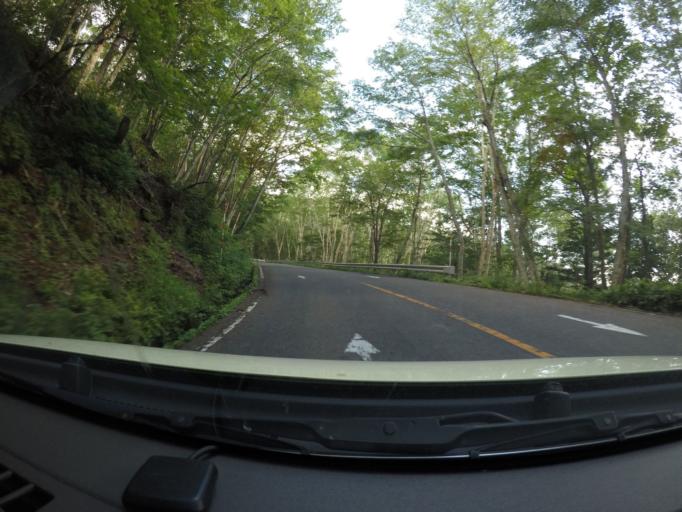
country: JP
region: Tochigi
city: Nikko
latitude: 36.8176
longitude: 139.3425
